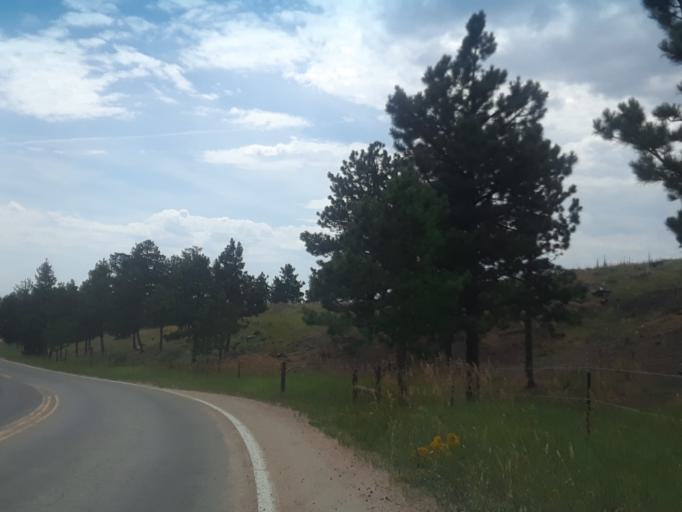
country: US
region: Colorado
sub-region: Boulder County
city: Boulder
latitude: 40.0549
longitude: -105.3614
